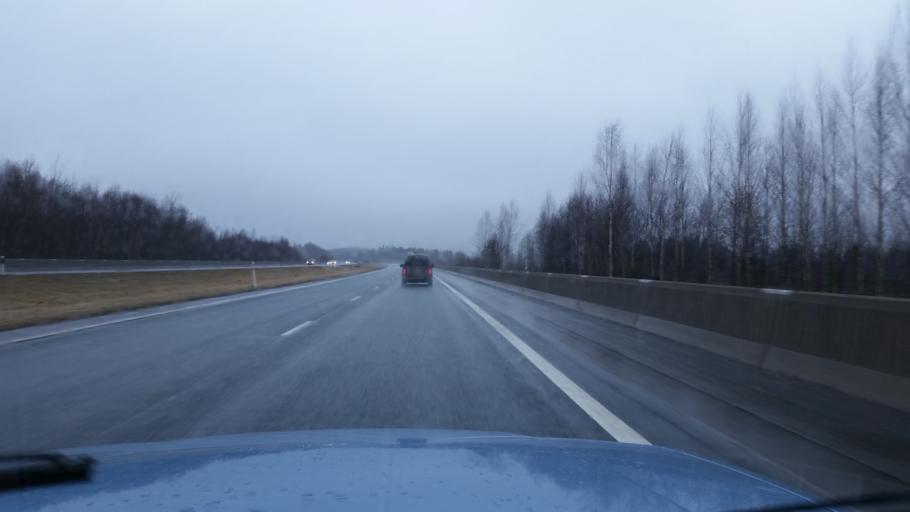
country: FI
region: Haeme
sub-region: Haemeenlinna
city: Parola
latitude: 61.0308
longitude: 24.3936
